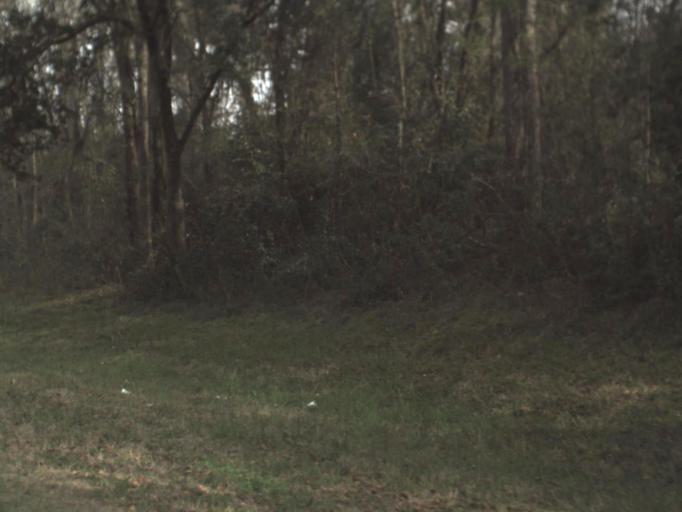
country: US
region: Florida
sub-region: Jefferson County
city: Monticello
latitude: 30.5288
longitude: -83.9825
